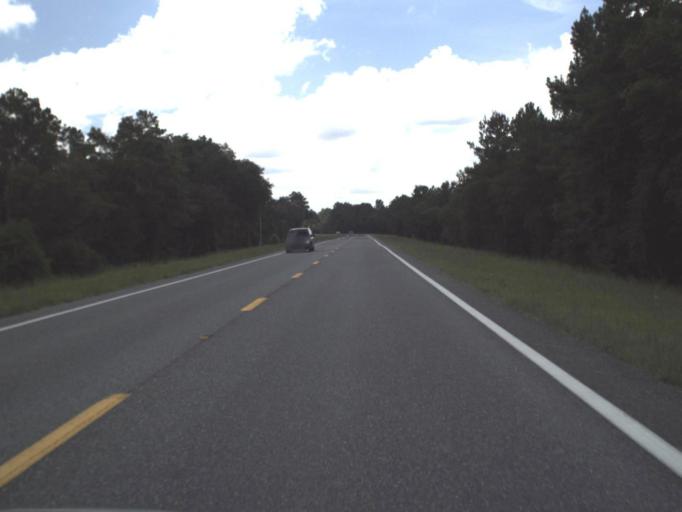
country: US
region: Florida
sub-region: Suwannee County
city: Wellborn
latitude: 30.3201
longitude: -82.7864
